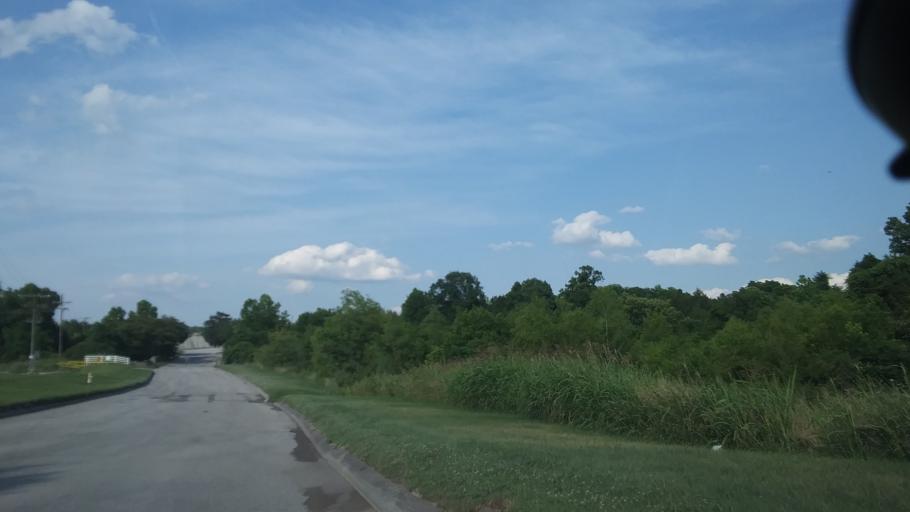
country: US
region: Tennessee
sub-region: Davidson County
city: Oak Hill
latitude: 36.0825
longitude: -86.6768
